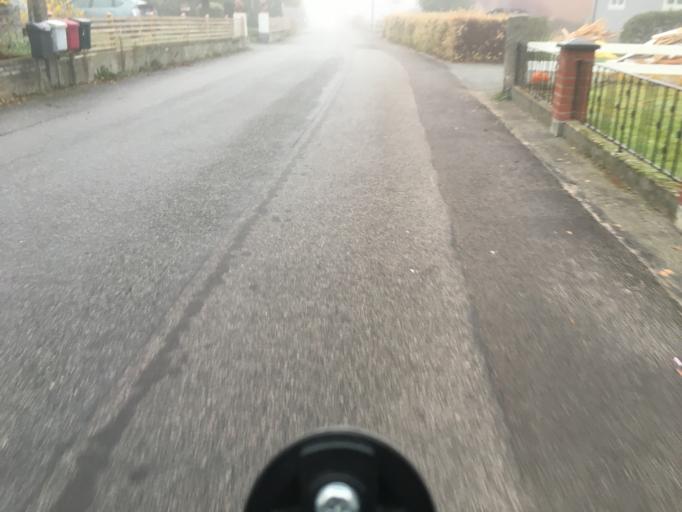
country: SE
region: Blekinge
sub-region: Karlshamns Kommun
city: Morrum
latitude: 56.1978
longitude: 14.7509
